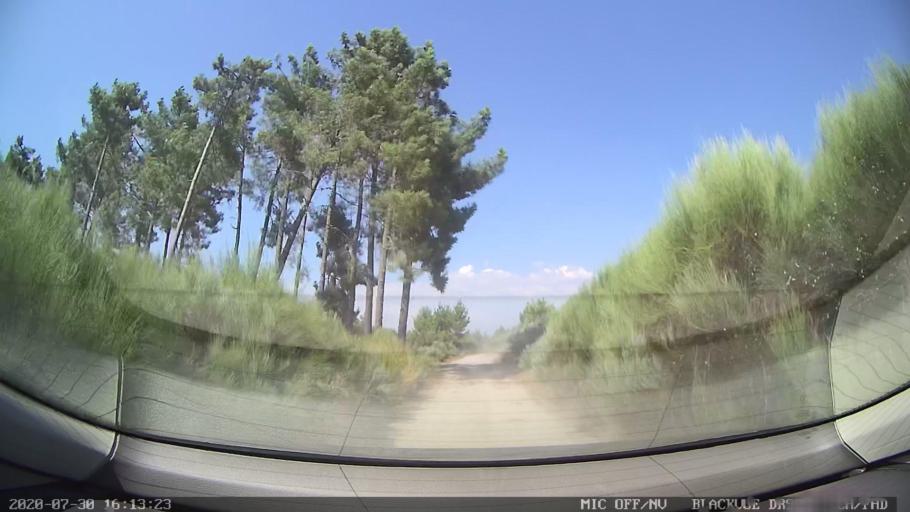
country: PT
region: Vila Real
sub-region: Murca
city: Murca
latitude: 41.3389
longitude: -7.4766
